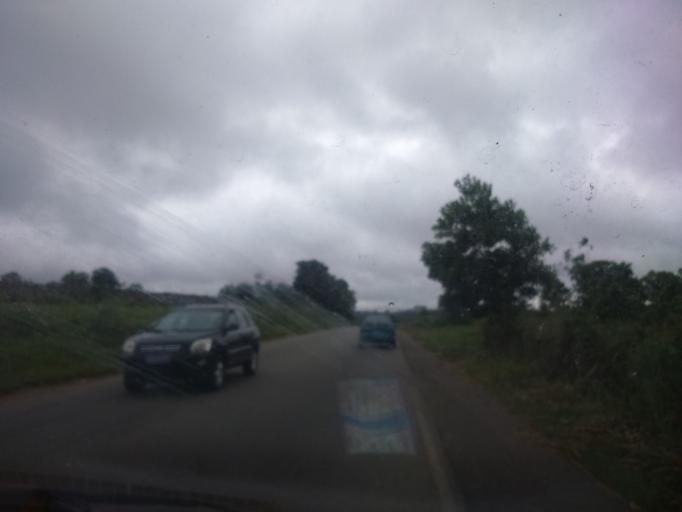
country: CI
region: Sud-Comoe
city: Bonoua
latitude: 5.2789
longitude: -3.5490
